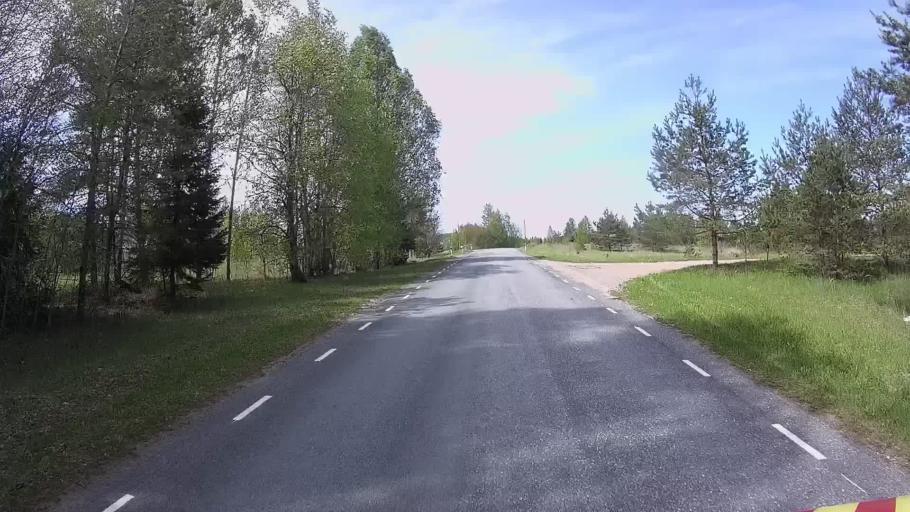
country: EE
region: Valgamaa
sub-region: Valga linn
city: Valga
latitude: 57.6566
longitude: 26.2921
